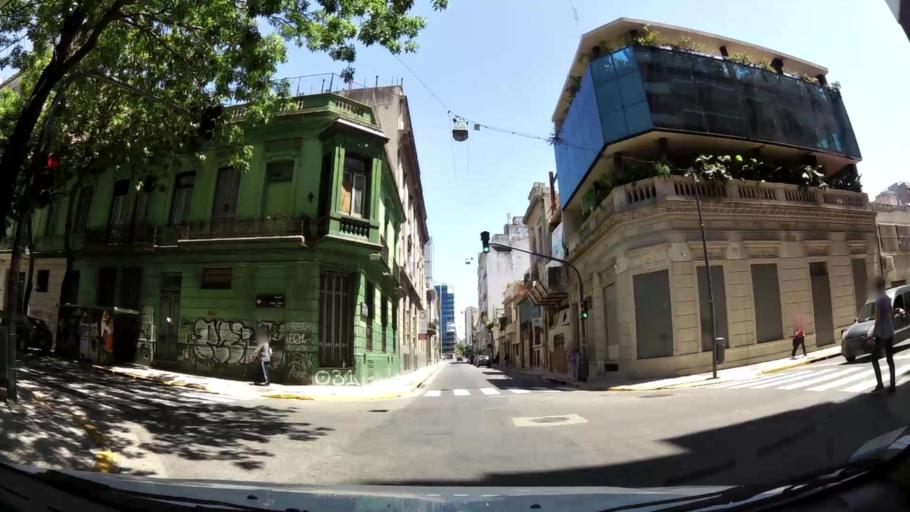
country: AR
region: Buenos Aires F.D.
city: Buenos Aires
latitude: -34.6197
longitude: -58.3785
